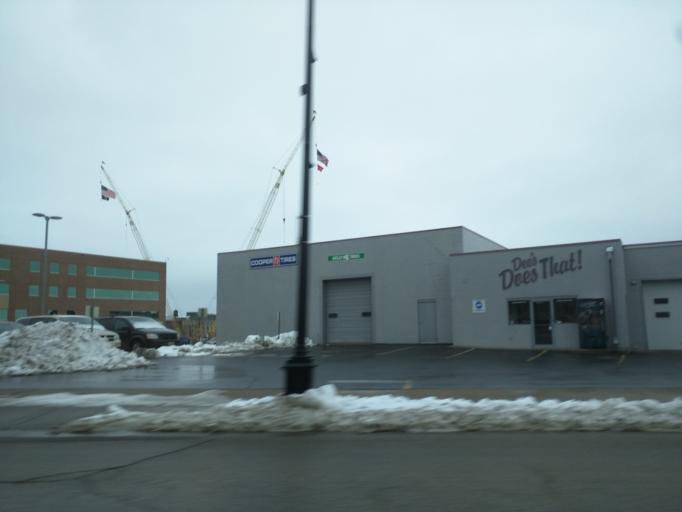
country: US
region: Wisconsin
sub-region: La Crosse County
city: La Crosse
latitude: 43.8159
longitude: -91.2490
